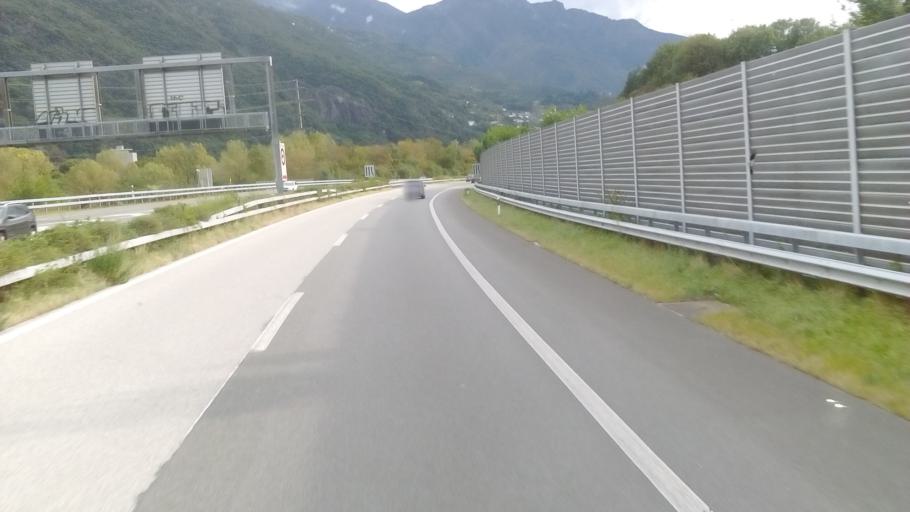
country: CH
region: Ticino
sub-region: Bellinzona District
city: Bellinzona
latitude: 46.2167
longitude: 9.0369
